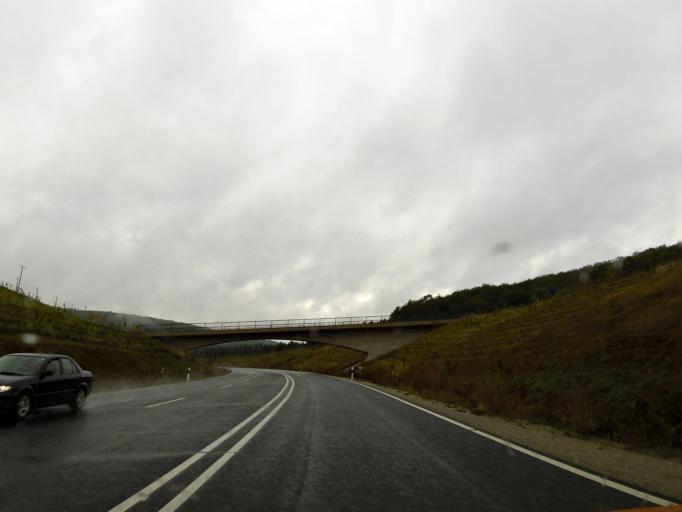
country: DE
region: Lower Saxony
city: Waake
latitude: 51.5617
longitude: 10.0550
